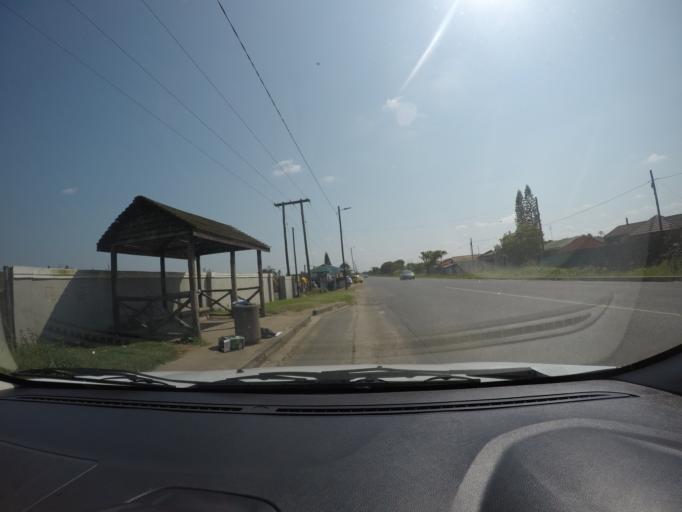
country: ZA
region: KwaZulu-Natal
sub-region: uThungulu District Municipality
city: eSikhawini
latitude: -28.8813
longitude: 31.8896
